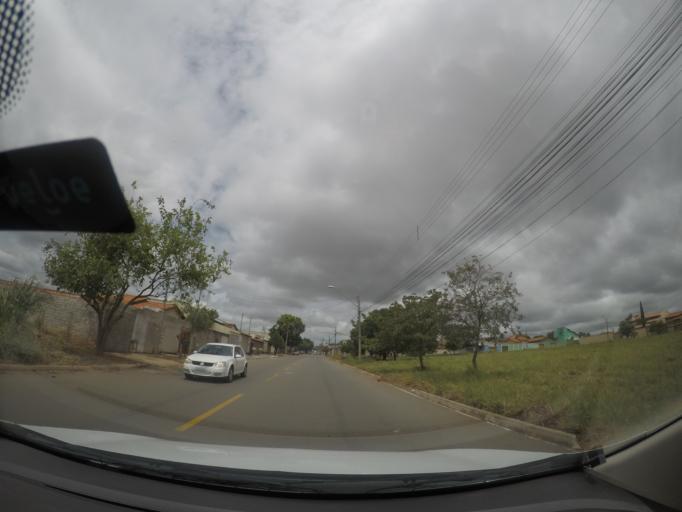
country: BR
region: Goias
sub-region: Goiania
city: Goiania
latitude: -16.7230
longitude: -49.3628
